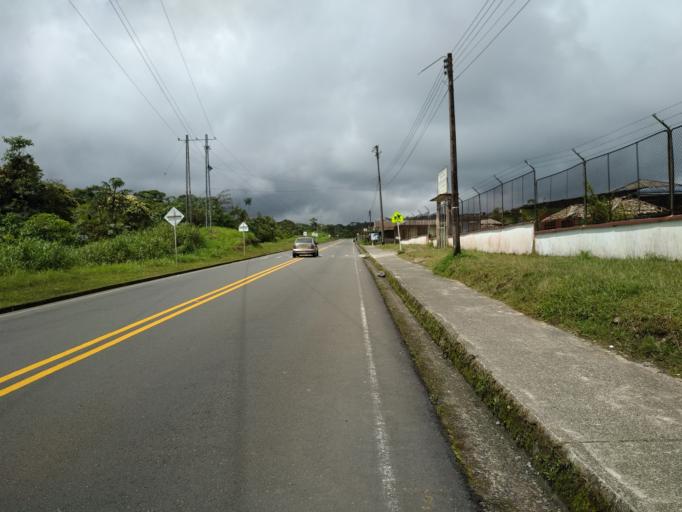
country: CO
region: Narino
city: Ricaurte
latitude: 1.3625
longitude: -78.1809
